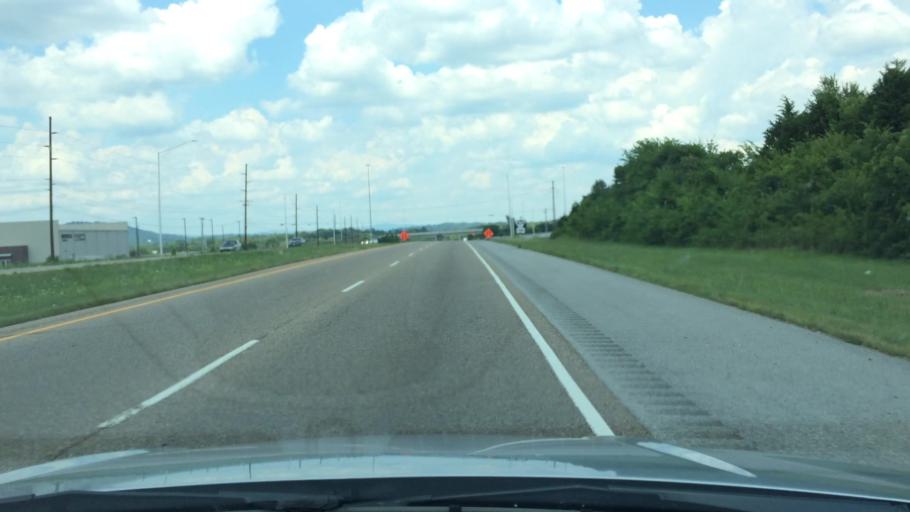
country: US
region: Tennessee
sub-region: Hamblen County
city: Morristown
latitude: 36.1709
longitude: -83.3510
